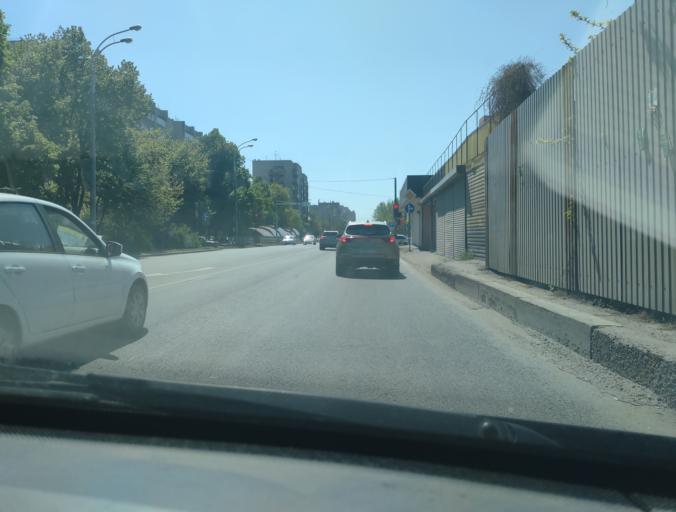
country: RU
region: Krasnodarskiy
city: Krasnodar
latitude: 45.0633
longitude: 39.0165
